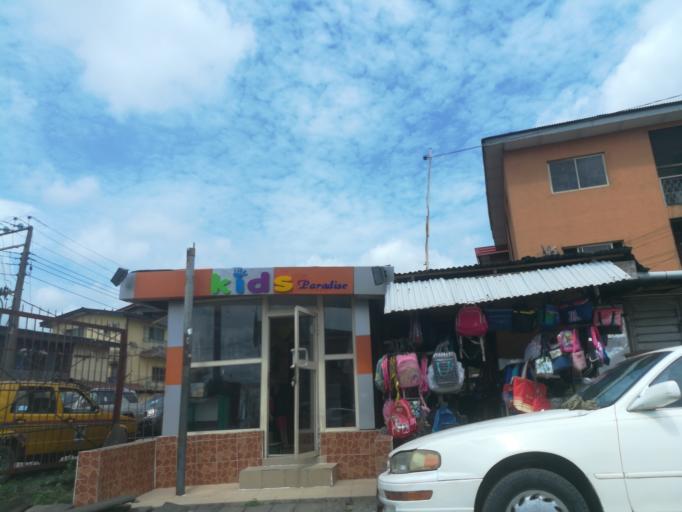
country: NG
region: Lagos
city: Somolu
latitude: 6.5265
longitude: 3.3810
